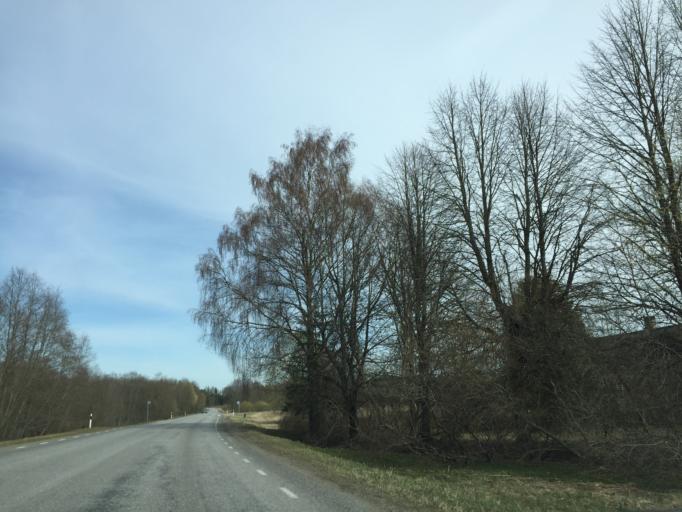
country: EE
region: Vorumaa
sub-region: Antsla vald
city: Vana-Antsla
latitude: 57.9326
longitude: 26.3503
